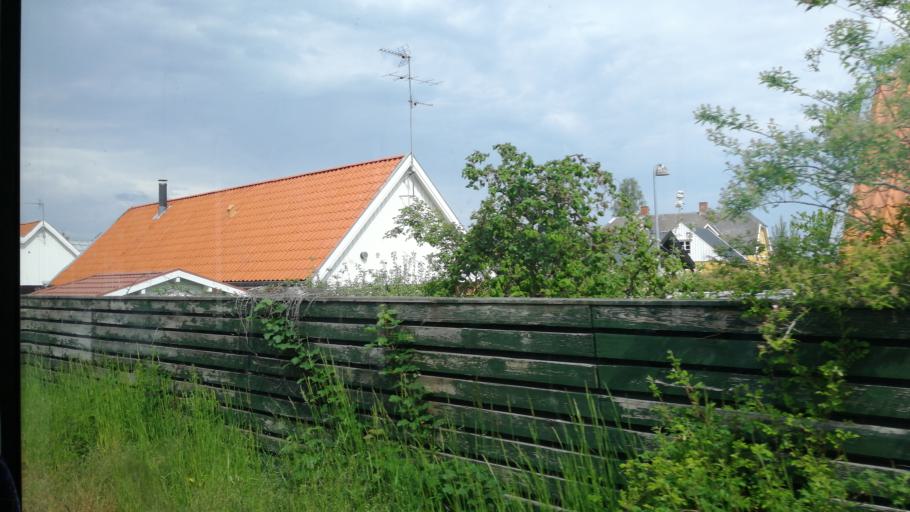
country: DK
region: Capital Region
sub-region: Helsingor Kommune
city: Hornbaek
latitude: 56.0973
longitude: 12.3906
